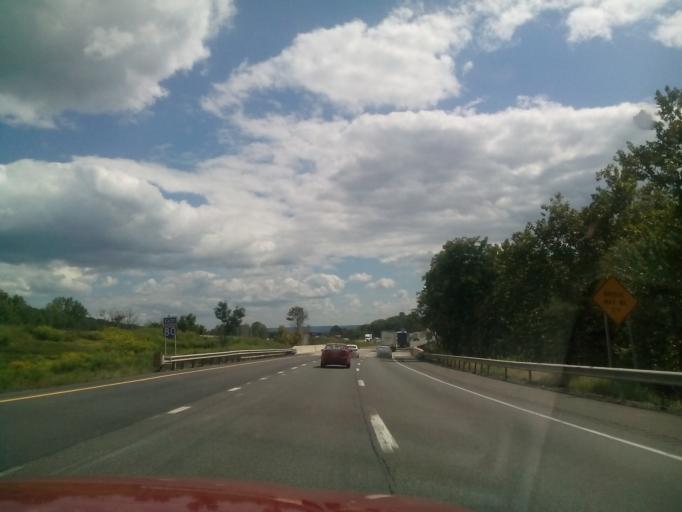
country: US
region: Pennsylvania
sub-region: Monroe County
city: Tannersville
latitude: 41.0523
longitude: -75.3170
